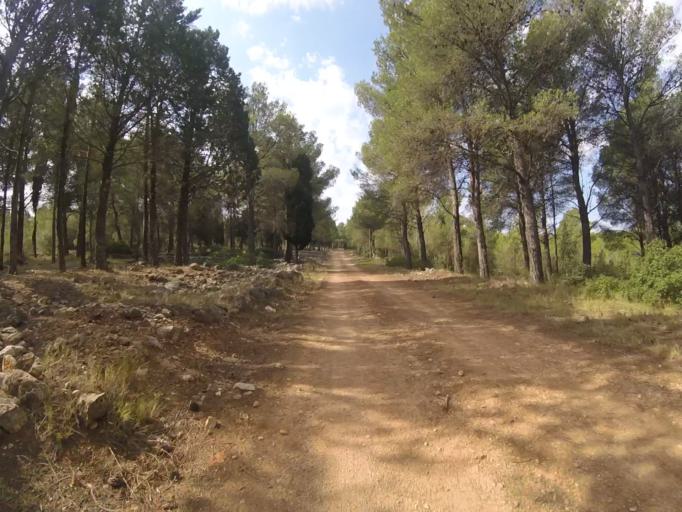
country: ES
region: Valencia
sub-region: Provincia de Castello
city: Alcala de Xivert
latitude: 40.3632
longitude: 0.2031
